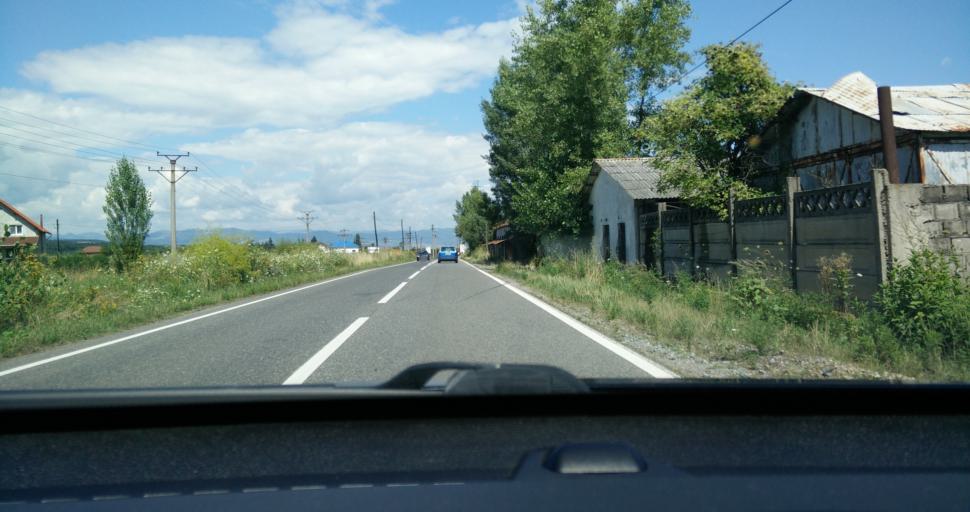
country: RO
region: Alba
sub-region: Comuna Sasciori
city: Sebesel
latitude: 45.9031
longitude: 23.5573
